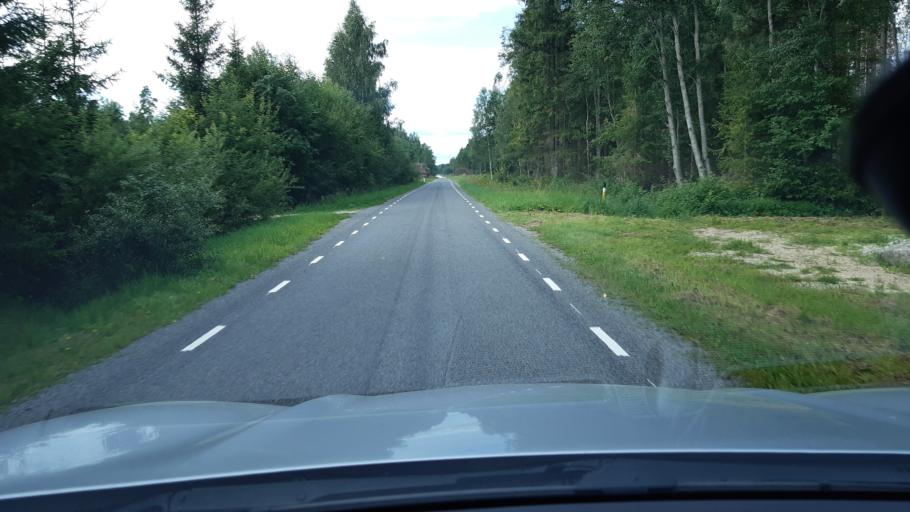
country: EE
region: Raplamaa
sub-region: Jaervakandi vald
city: Jarvakandi
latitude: 58.7512
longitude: 24.9181
